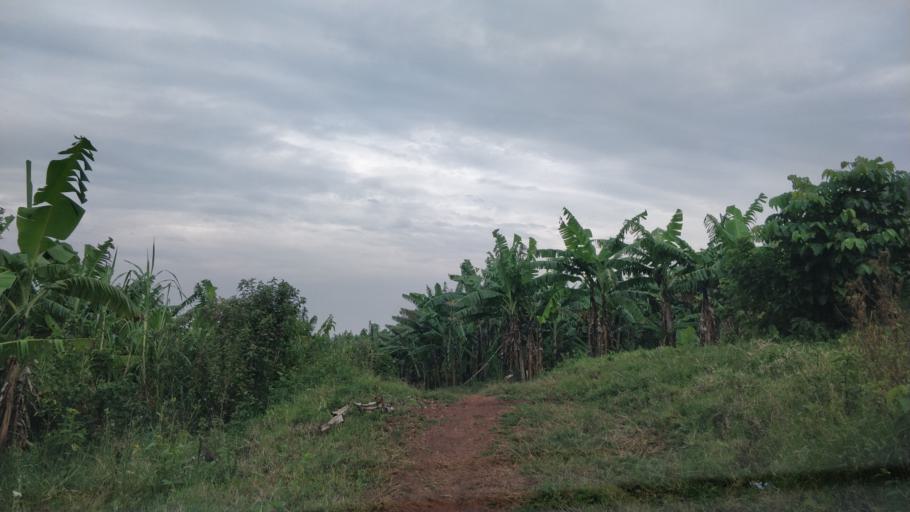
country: UG
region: Western Region
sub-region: Sheema District
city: Kibingo
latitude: -0.7028
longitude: 30.4013
